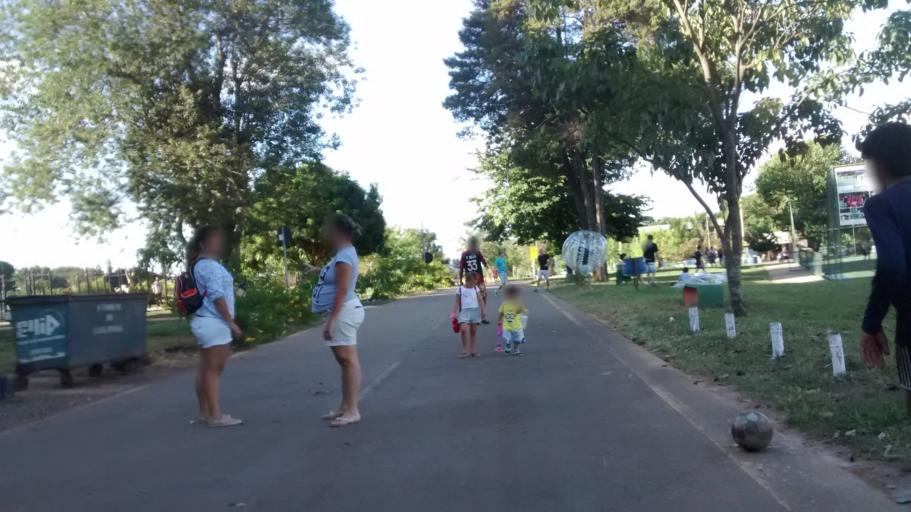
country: BR
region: Federal District
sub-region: Brasilia
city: Brasilia
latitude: -15.8296
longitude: -48.0217
